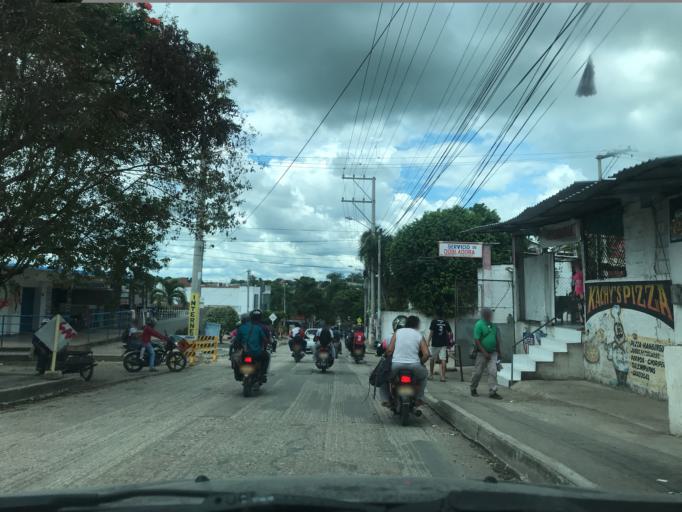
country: CO
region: Sucre
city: Sincelejo
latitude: 9.3104
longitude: -75.3984
